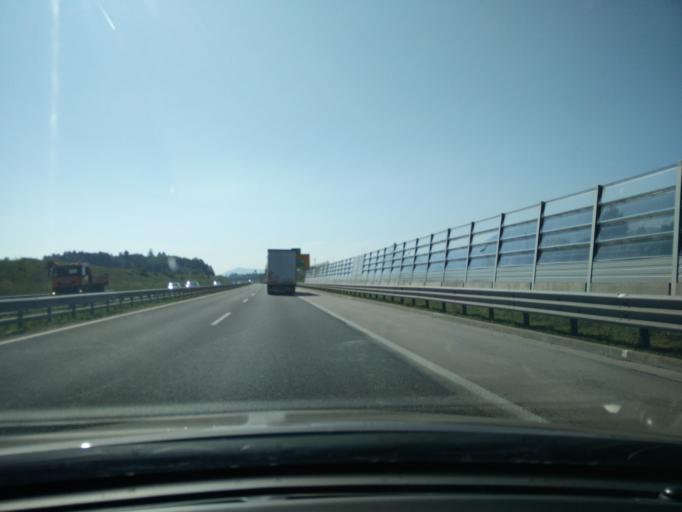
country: SI
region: Radovljica
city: Radovljica
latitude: 46.3483
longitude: 14.1802
